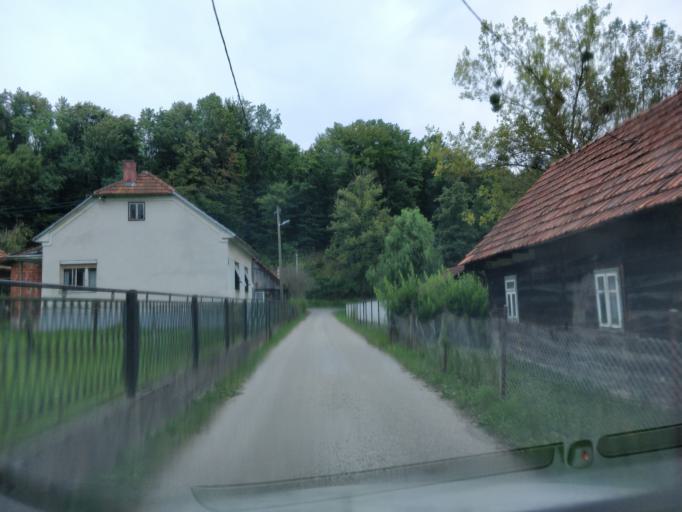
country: HR
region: Krapinsko-Zagorska
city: Oroslavje
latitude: 45.9394
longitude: 15.9182
